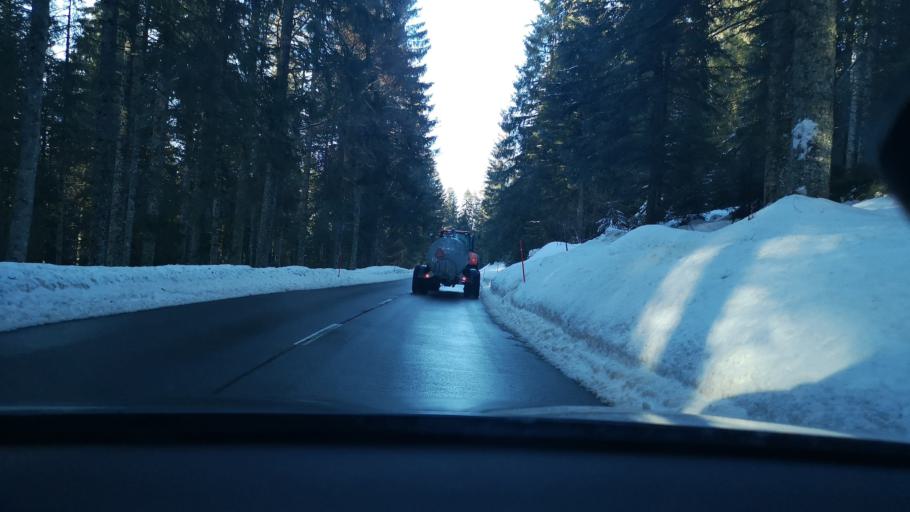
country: CH
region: Neuchatel
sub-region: Val-de-Travers District
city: Fleurier
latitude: 46.9419
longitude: 6.5258
